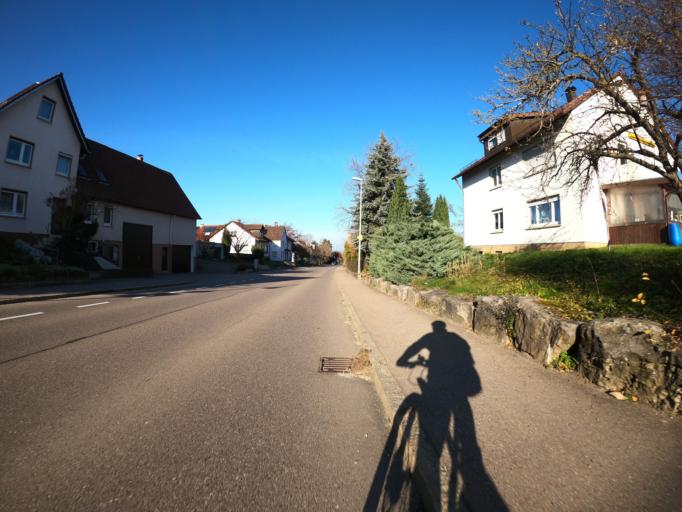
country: DE
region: Baden-Wuerttemberg
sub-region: Regierungsbezirk Stuttgart
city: Gammelshausen
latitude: 48.6413
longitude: 9.6505
